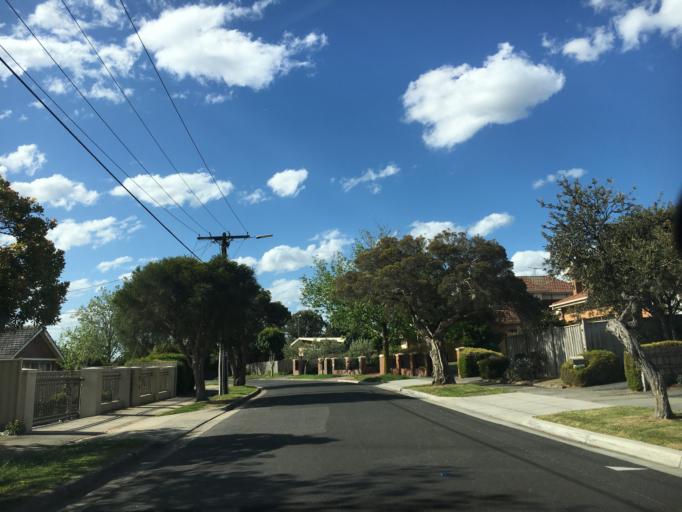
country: AU
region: Victoria
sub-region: Whitehorse
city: Vermont South
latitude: -37.8868
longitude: 145.1699
